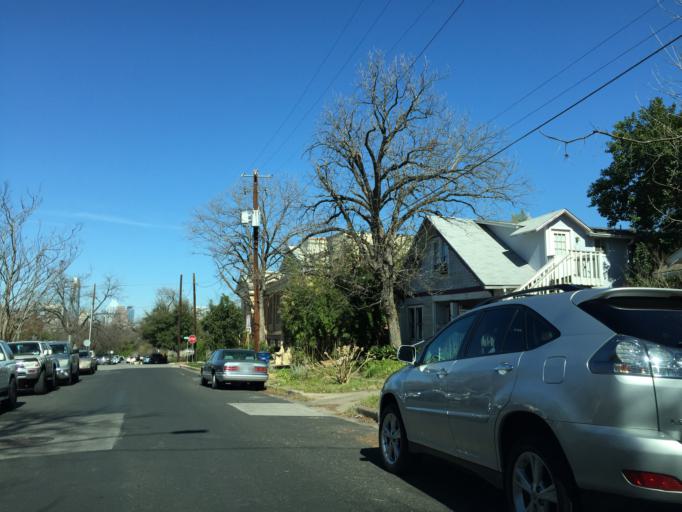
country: US
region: Texas
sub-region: Travis County
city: Austin
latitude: 30.2470
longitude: -97.7494
